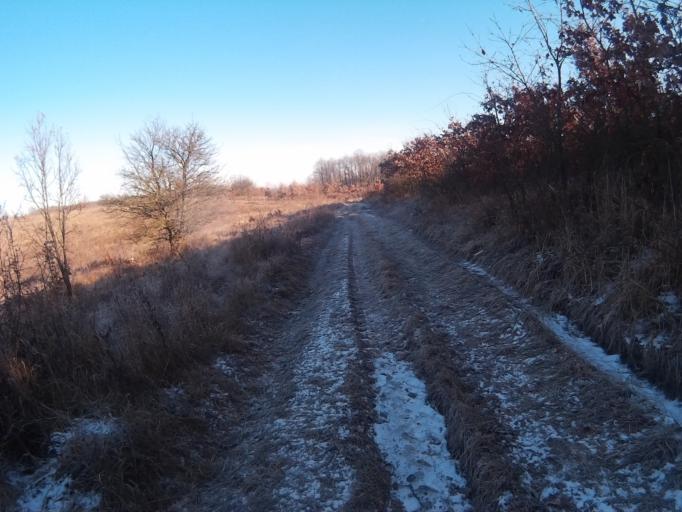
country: HU
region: Borsod-Abauj-Zemplen
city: Putnok
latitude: 48.3766
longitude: 20.4495
